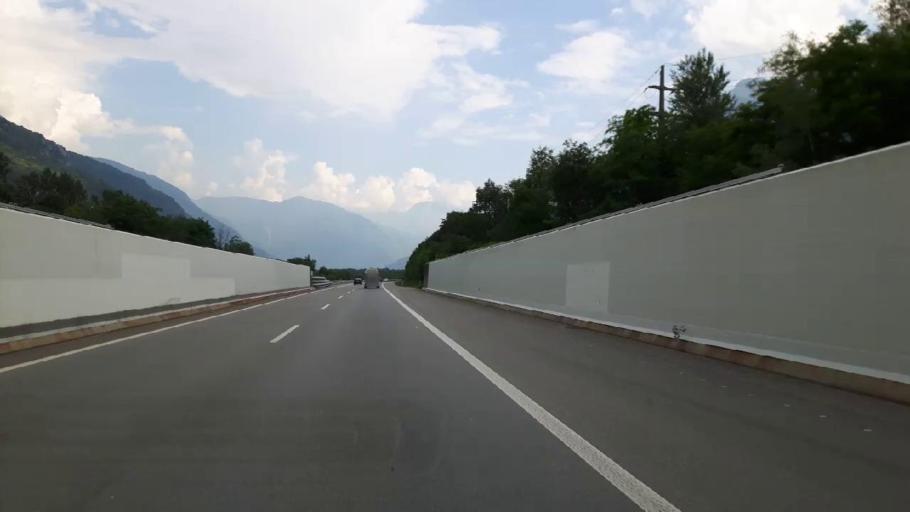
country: CH
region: Ticino
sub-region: Riviera District
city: Lodrino
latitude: 46.3024
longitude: 8.9860
